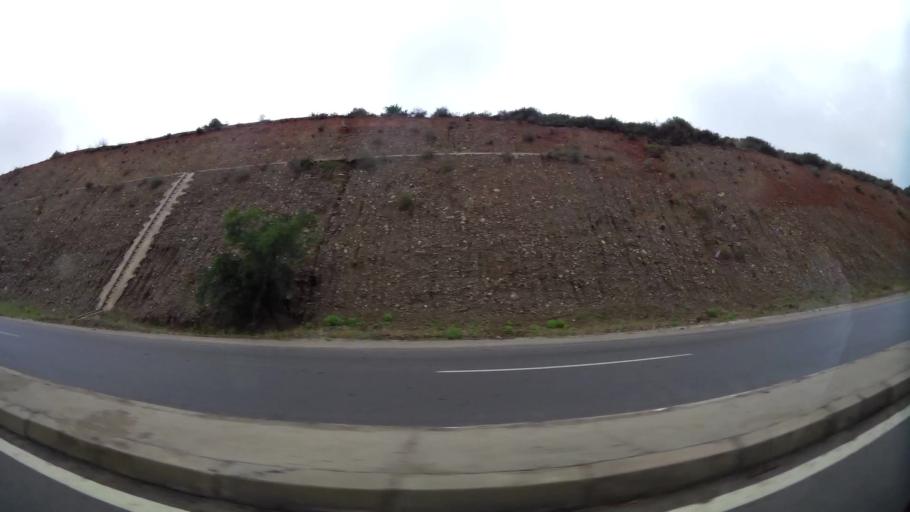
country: MA
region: Taza-Al Hoceima-Taounate
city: Imzourene
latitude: 35.1894
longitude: -3.8863
